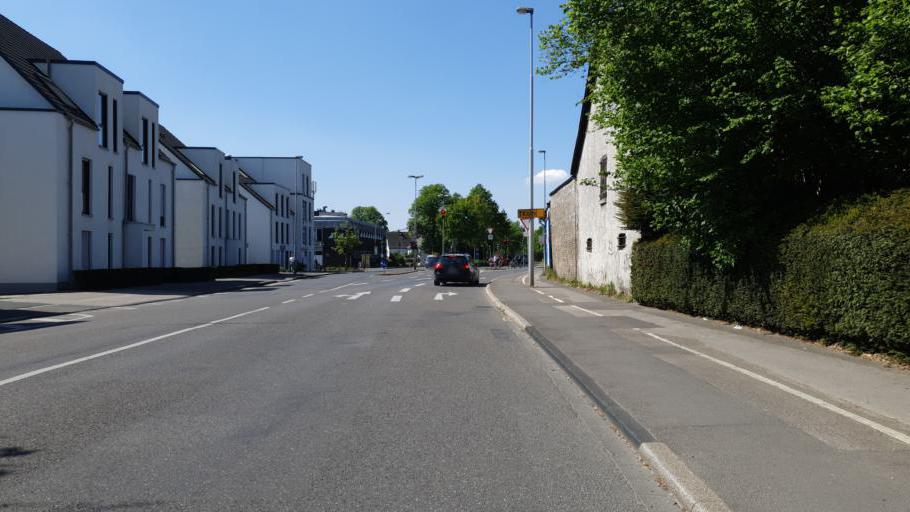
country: DE
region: North Rhine-Westphalia
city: Opladen
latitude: 51.0363
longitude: 7.0539
